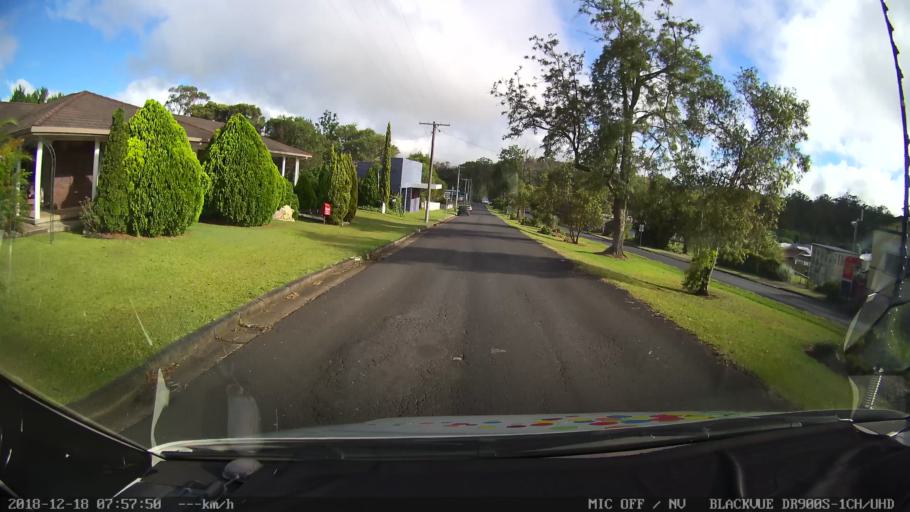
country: AU
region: New South Wales
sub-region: Kyogle
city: Kyogle
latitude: -28.3911
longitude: 152.6120
